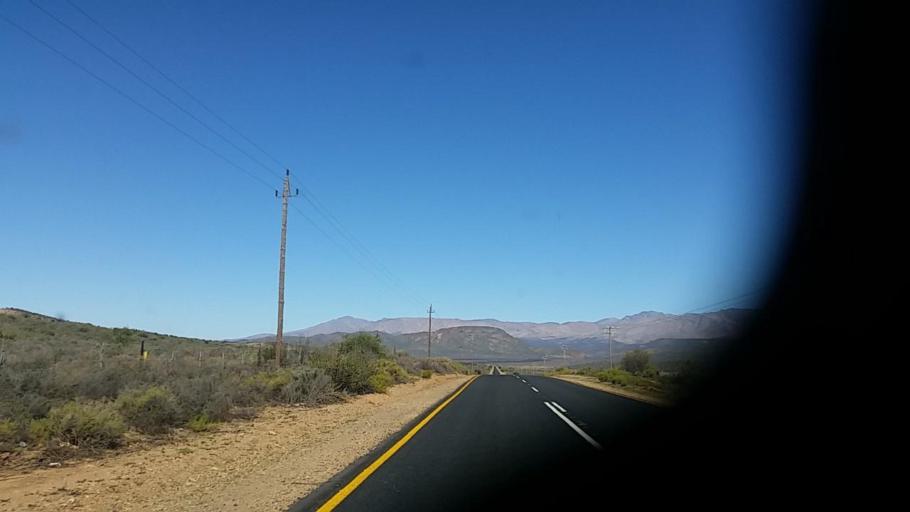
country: ZA
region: Western Cape
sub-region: Eden District Municipality
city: Oudtshoorn
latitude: -33.4849
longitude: 22.6621
